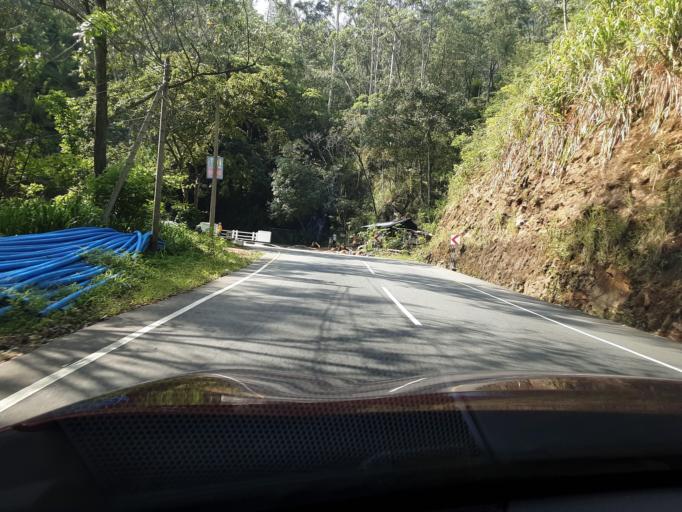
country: LK
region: Uva
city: Badulla
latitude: 6.9593
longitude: 81.1036
